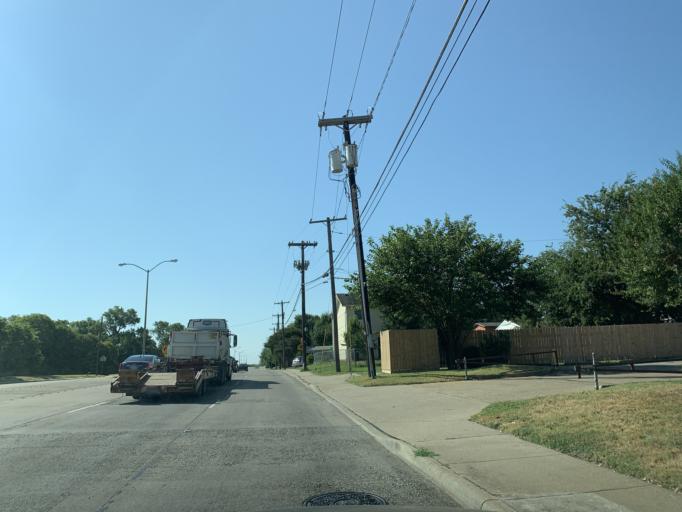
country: US
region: Texas
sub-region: Dallas County
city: Hutchins
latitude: 32.6699
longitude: -96.7611
